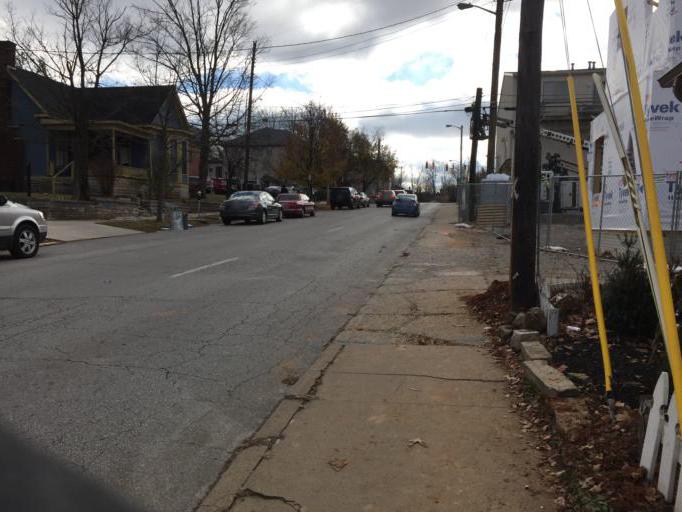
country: US
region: Indiana
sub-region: Monroe County
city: Bloomington
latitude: 39.1654
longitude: -86.5284
